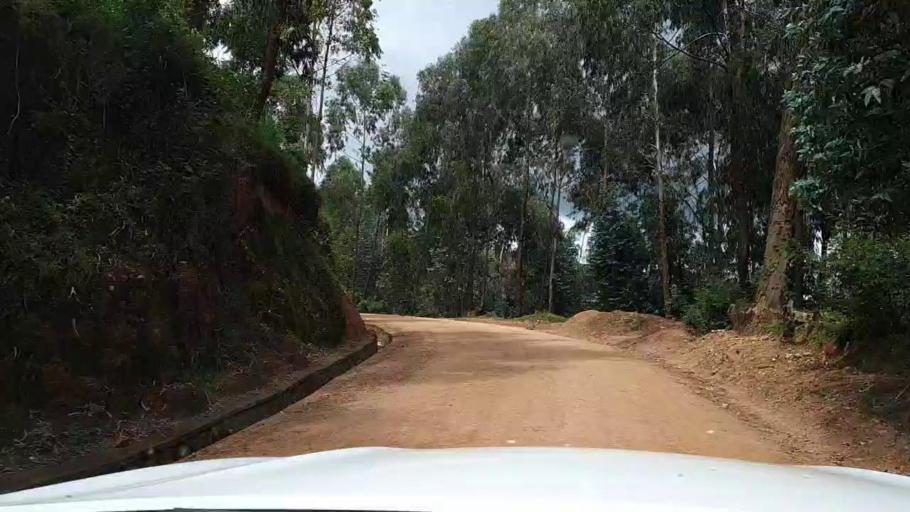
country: RW
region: Southern Province
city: Nzega
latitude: -2.4282
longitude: 29.4416
